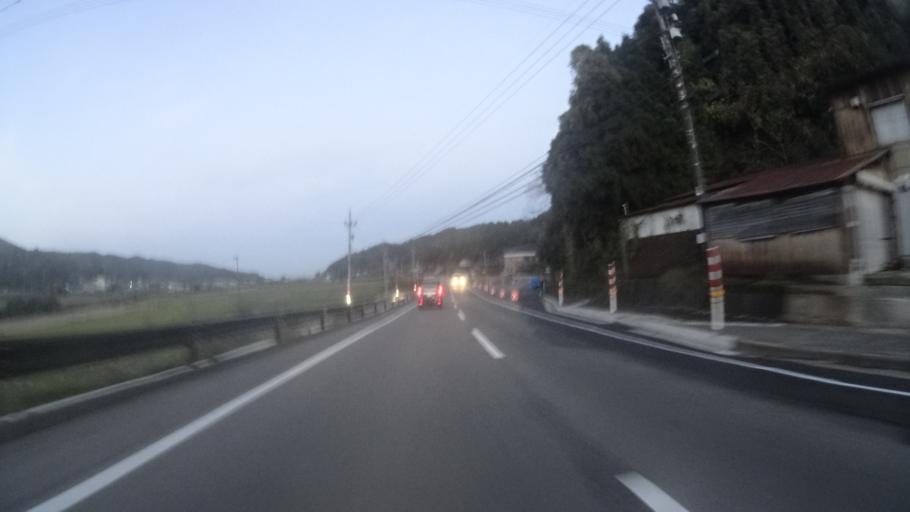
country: JP
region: Ishikawa
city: Nanao
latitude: 37.3677
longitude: 136.8715
